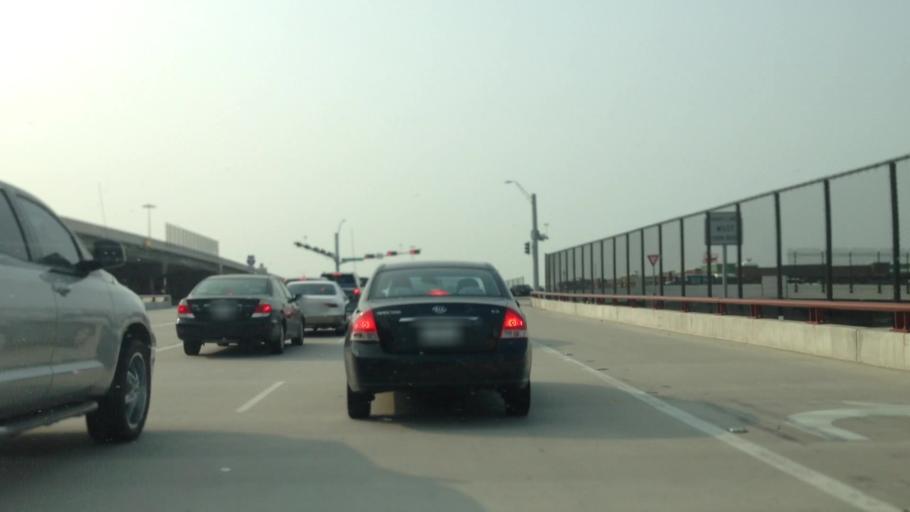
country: US
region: Texas
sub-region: Dallas County
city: Carrollton
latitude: 32.9527
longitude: -96.9094
